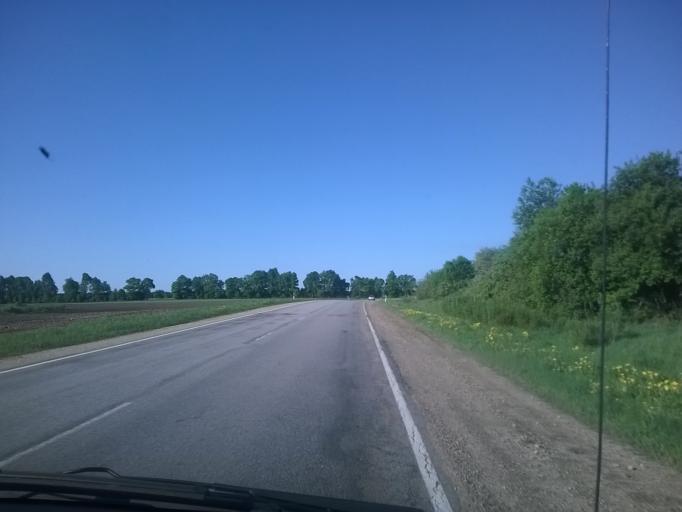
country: LV
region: Valkas Rajons
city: Valka
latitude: 57.7497
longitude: 25.9643
